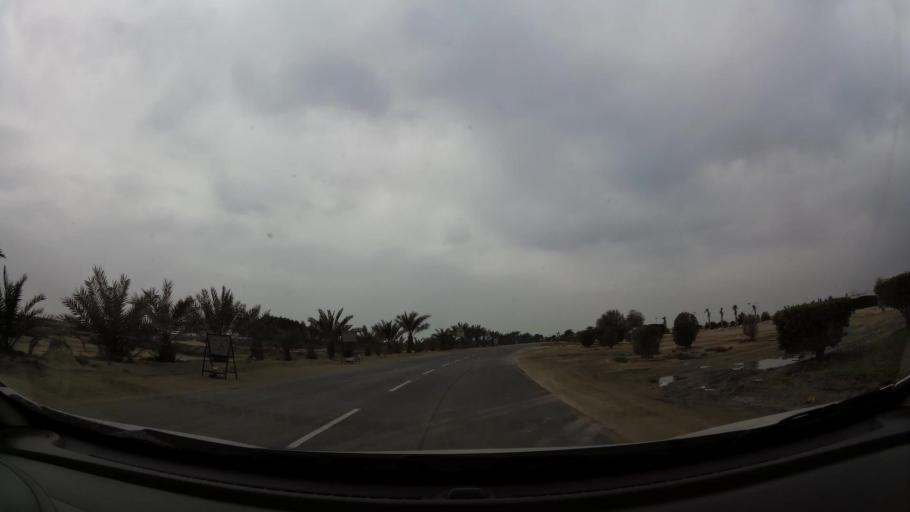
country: BH
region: Central Governorate
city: Dar Kulayb
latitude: 25.9947
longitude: 50.4674
